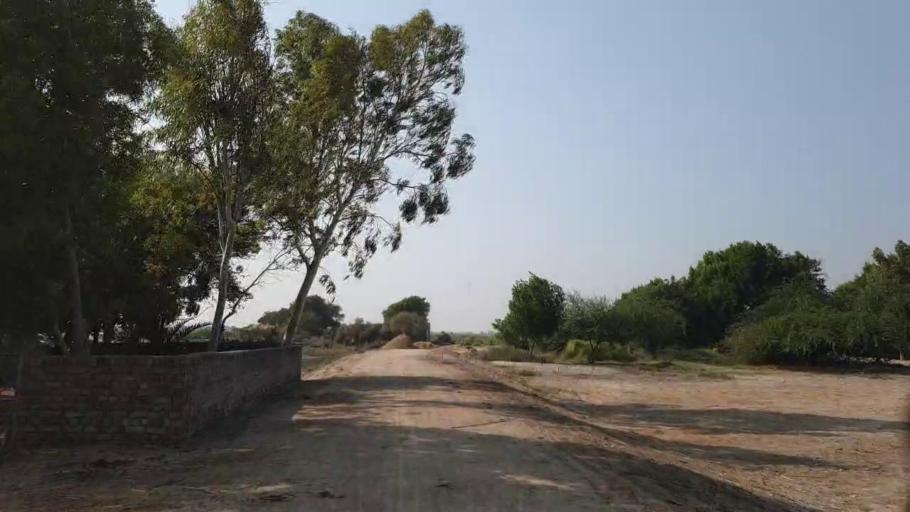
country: PK
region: Sindh
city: Bulri
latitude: 24.9462
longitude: 68.3863
